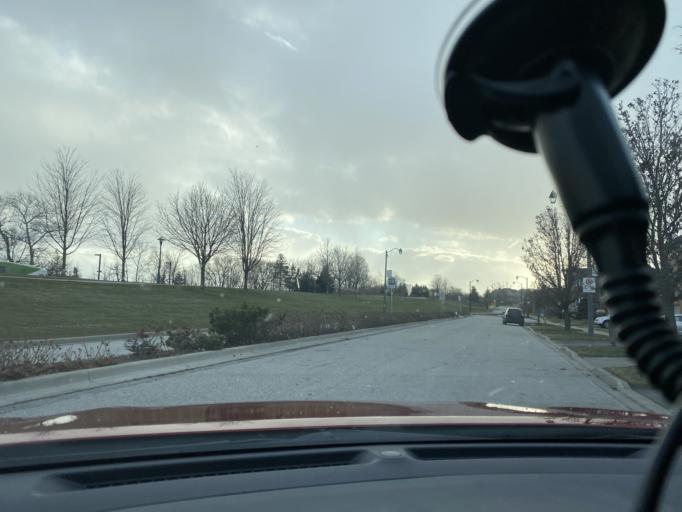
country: CA
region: Ontario
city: Pickering
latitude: 43.7790
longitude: -79.1322
